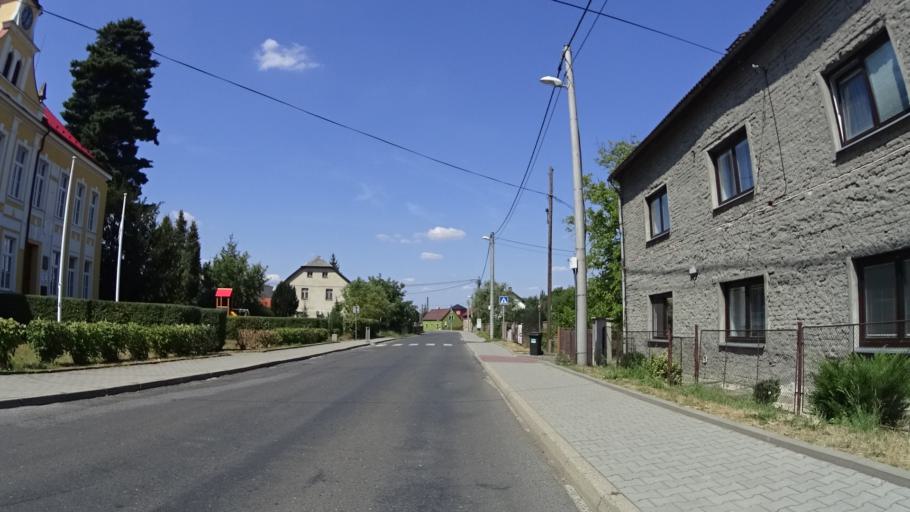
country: CZ
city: Hradek nad Nisou
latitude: 50.8471
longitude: 14.8519
